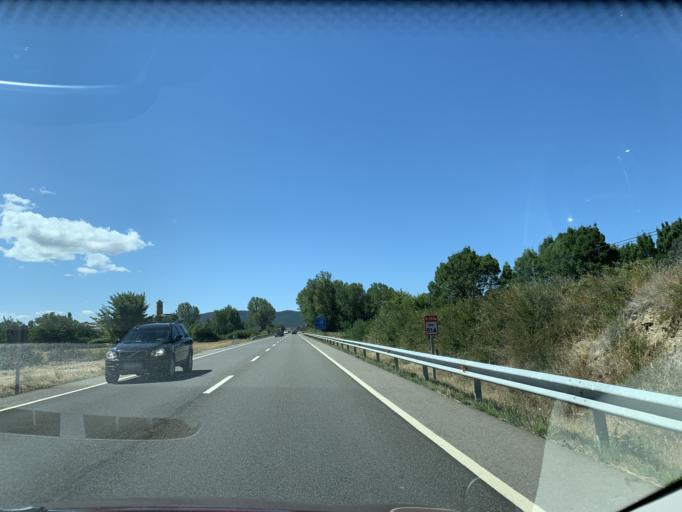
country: ES
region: Aragon
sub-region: Provincia de Huesca
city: Sabinanigo
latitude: 42.5536
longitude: -0.3412
